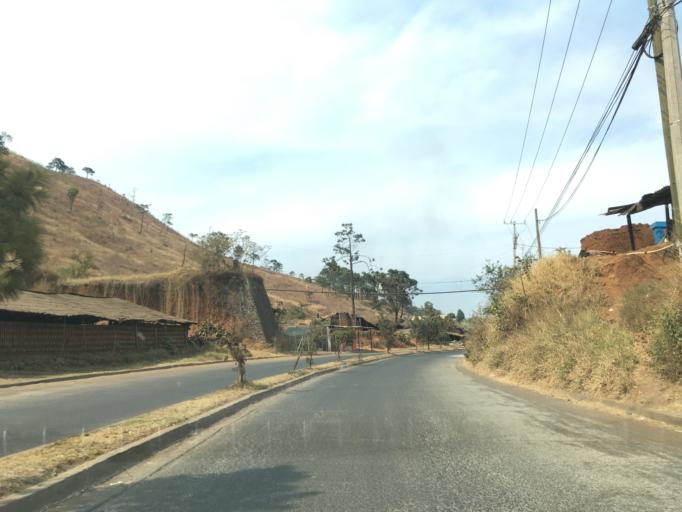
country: MX
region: Michoacan
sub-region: Uruapan
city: Uruapan
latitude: 19.3823
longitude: -102.0767
